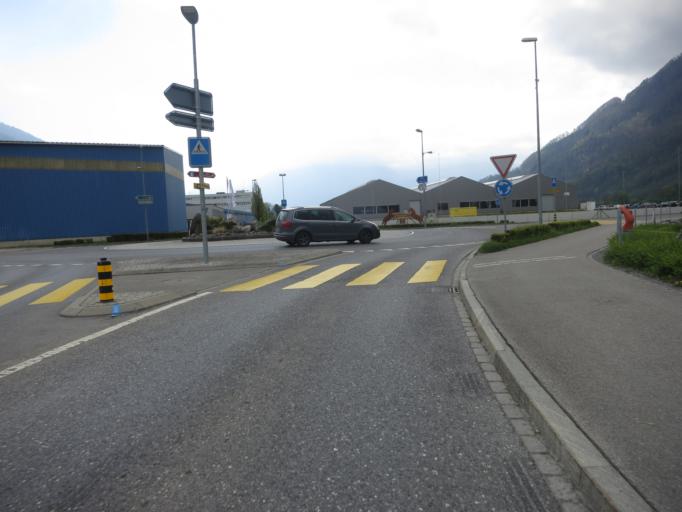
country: CH
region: Glarus
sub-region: Glarus
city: Bilten
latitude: 47.1513
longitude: 9.0287
